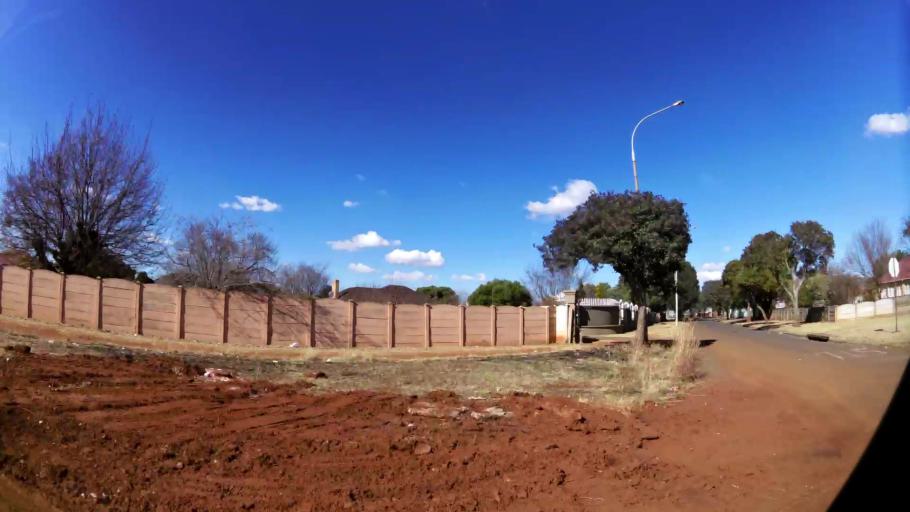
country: ZA
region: Gauteng
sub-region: West Rand District Municipality
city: Carletonville
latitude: -26.3610
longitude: 27.3999
